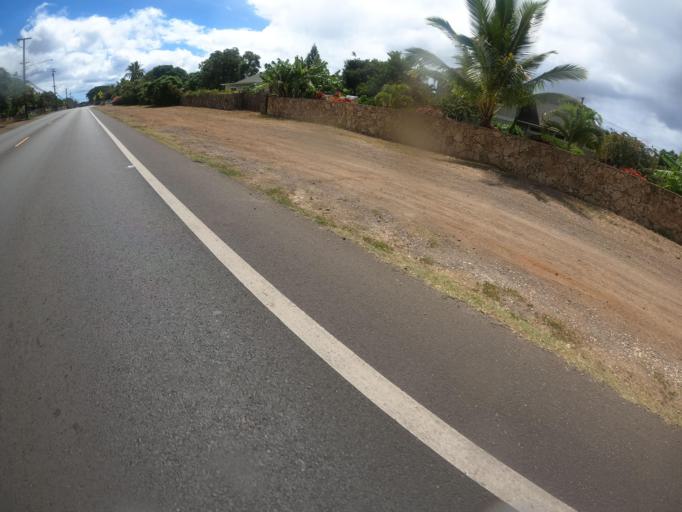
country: US
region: Hawaii
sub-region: Honolulu County
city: Makaha
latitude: 21.4729
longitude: -158.2176
